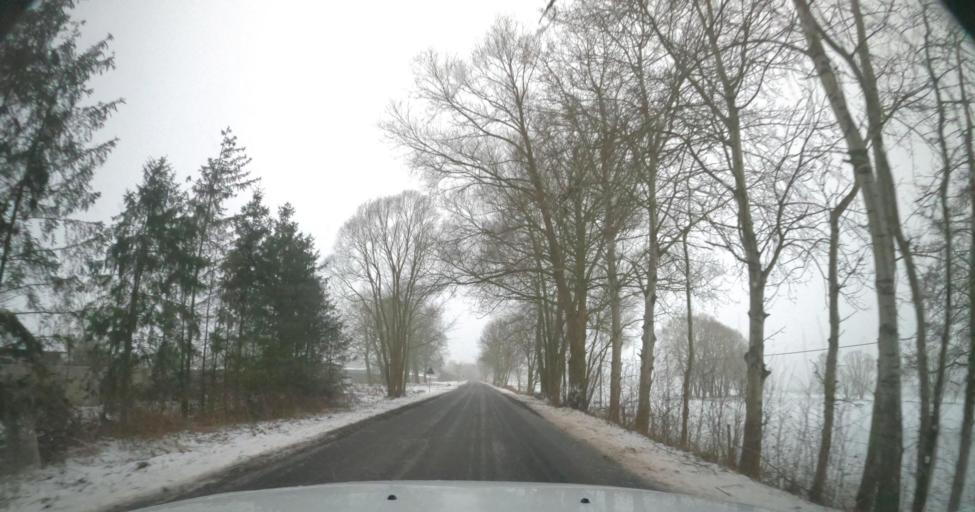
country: PL
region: West Pomeranian Voivodeship
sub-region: Powiat goleniowski
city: Goleniow
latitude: 53.5744
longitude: 14.7263
